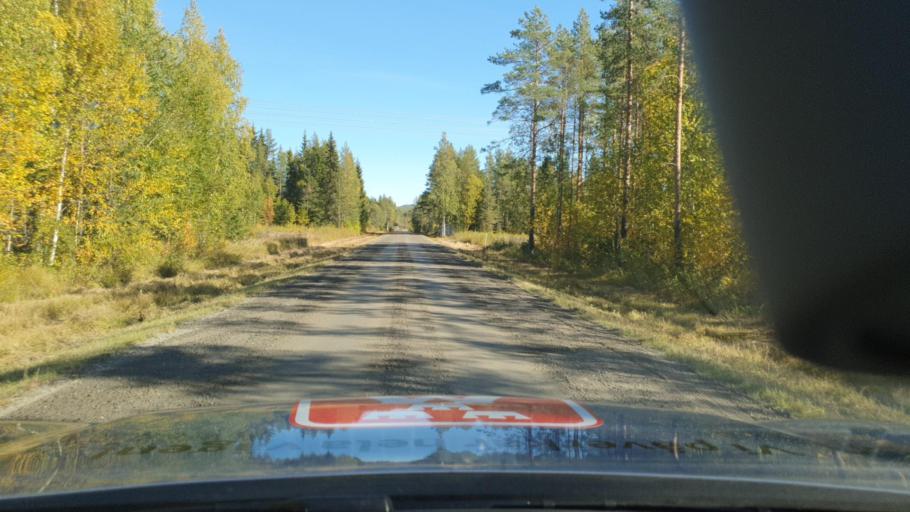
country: SE
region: Norrbotten
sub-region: Bodens Kommun
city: Boden
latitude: 66.0619
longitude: 21.3951
